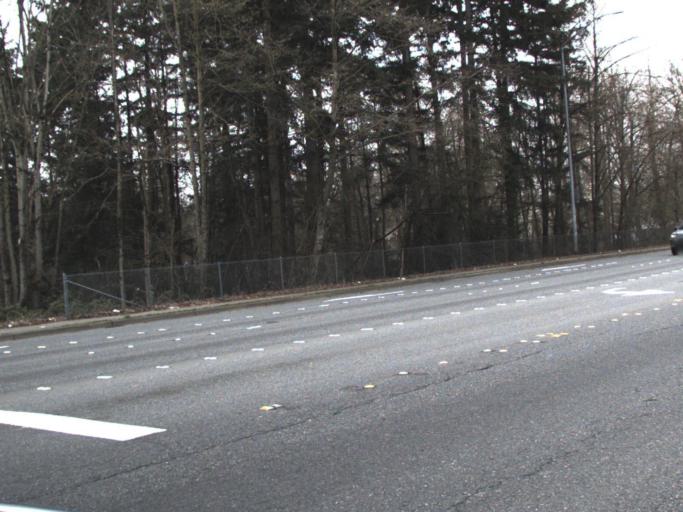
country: US
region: Washington
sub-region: King County
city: Lea Hill
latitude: 47.3633
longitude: -122.1765
